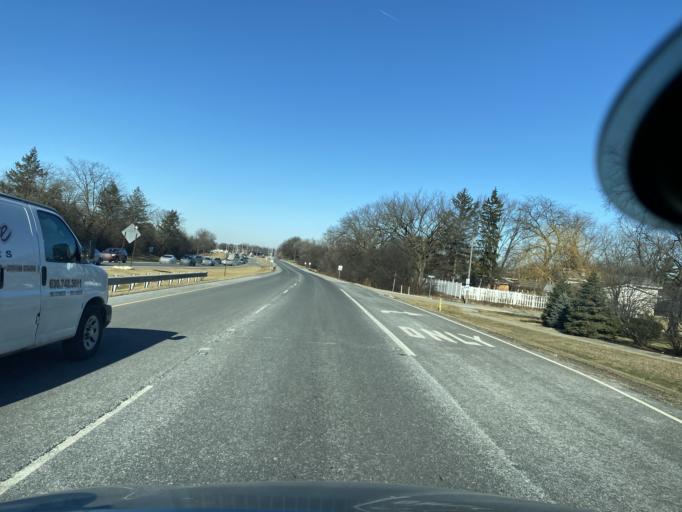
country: US
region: Illinois
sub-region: DuPage County
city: Willowbrook
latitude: 41.7681
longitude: -87.9450
